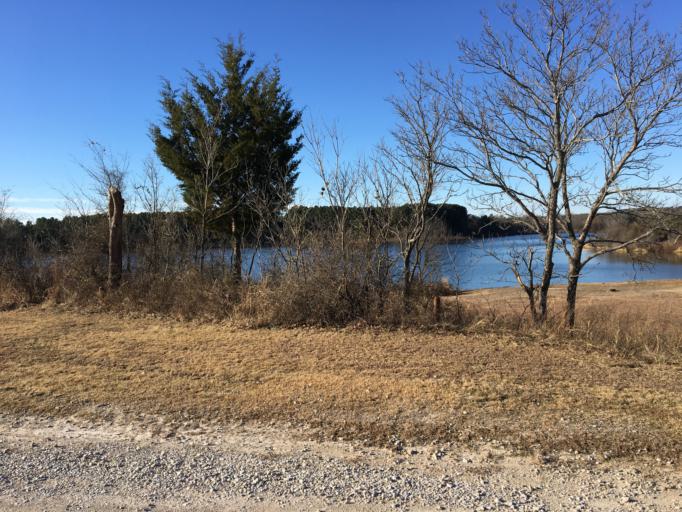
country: US
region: Texas
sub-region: Wise County
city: Alvord
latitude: 33.3450
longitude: -97.5950
